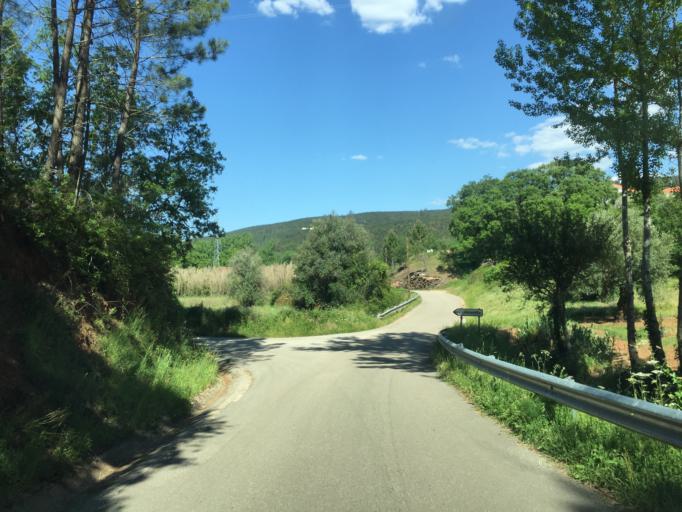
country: PT
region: Leiria
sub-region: Alvaiazere
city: Alvaiazere
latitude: 39.8469
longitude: -8.3516
